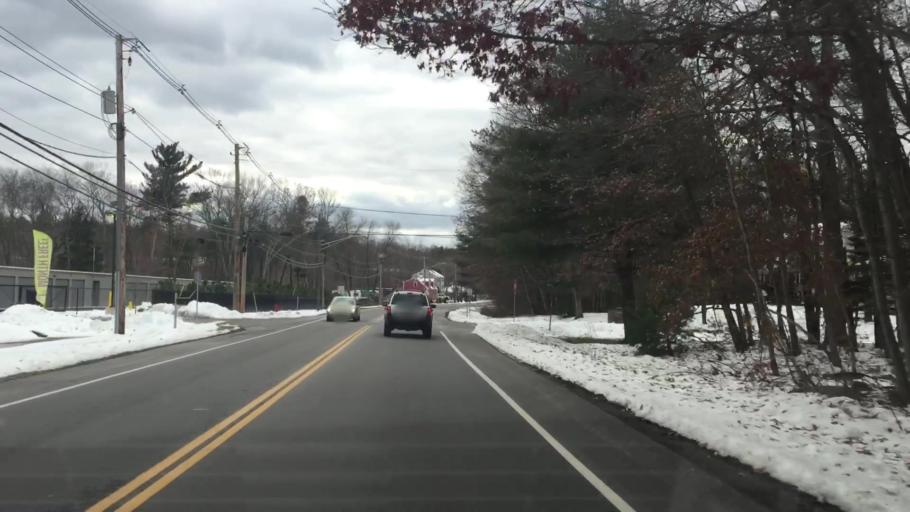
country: US
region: New Hampshire
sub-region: Rockingham County
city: Salem
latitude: 42.7631
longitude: -71.2518
